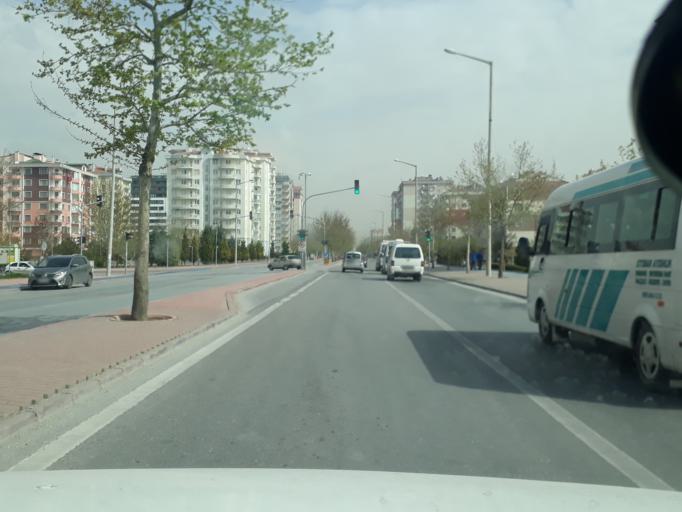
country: TR
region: Konya
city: Selcuklu
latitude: 37.9418
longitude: 32.4931
